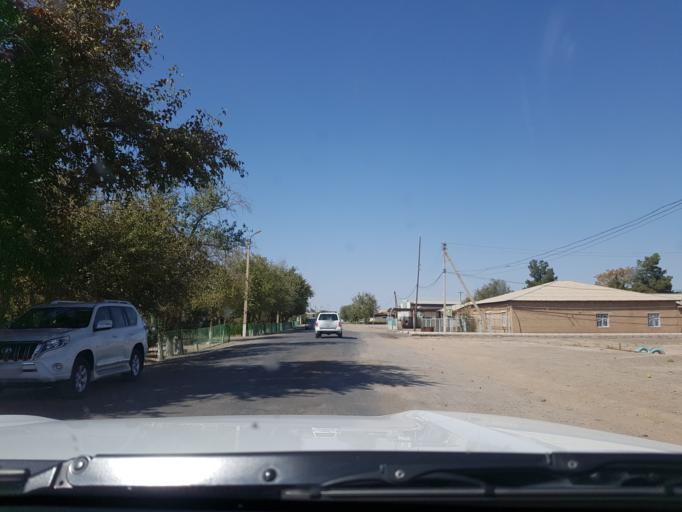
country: IR
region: Razavi Khorasan
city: Sarakhs
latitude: 36.5199
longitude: 61.2190
